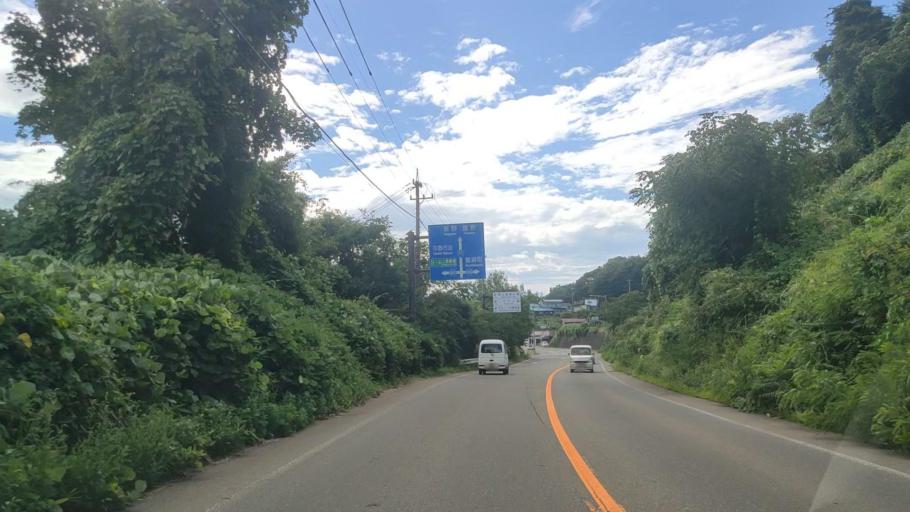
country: JP
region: Nagano
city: Nakano
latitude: 36.7578
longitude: 138.3175
